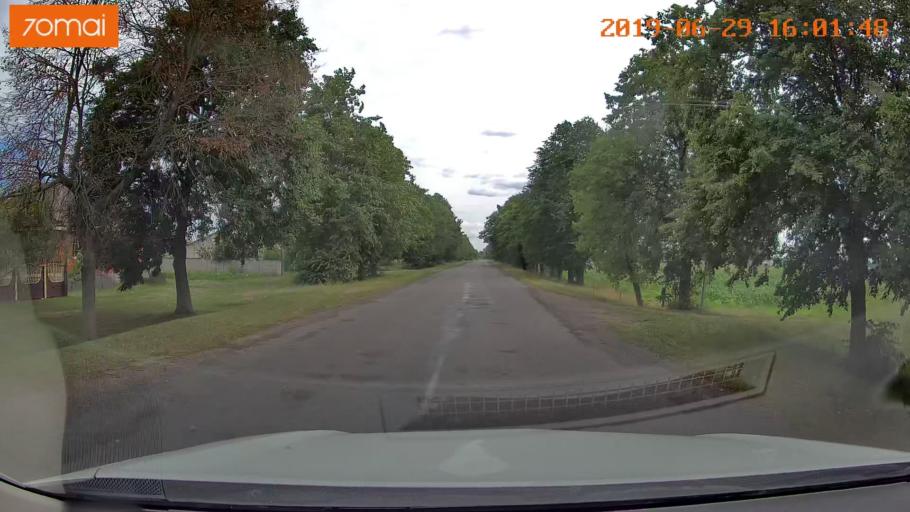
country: BY
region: Brest
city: Luninyets
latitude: 52.2427
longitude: 27.0162
